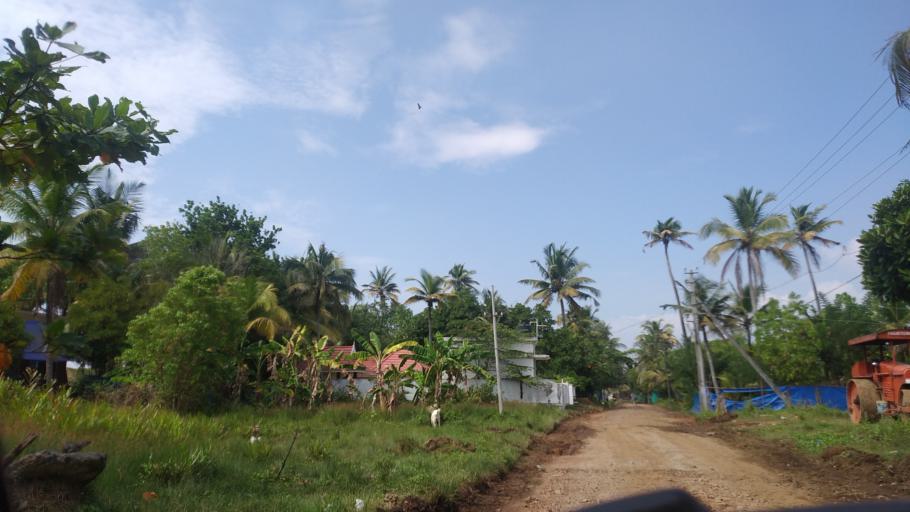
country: IN
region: Kerala
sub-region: Ernakulam
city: Elur
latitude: 10.0572
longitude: 76.2014
